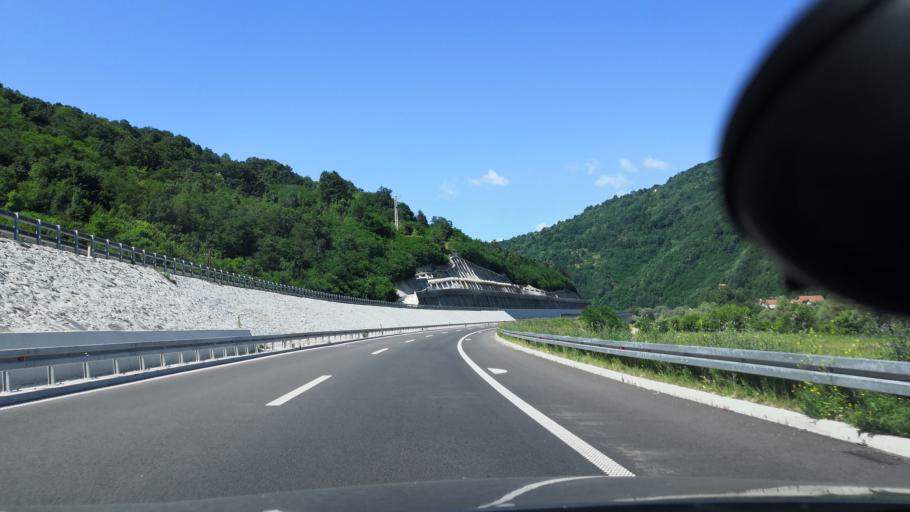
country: RS
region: Central Serbia
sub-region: Pcinjski Okrug
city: Vladicin Han
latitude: 42.7738
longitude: 22.0863
